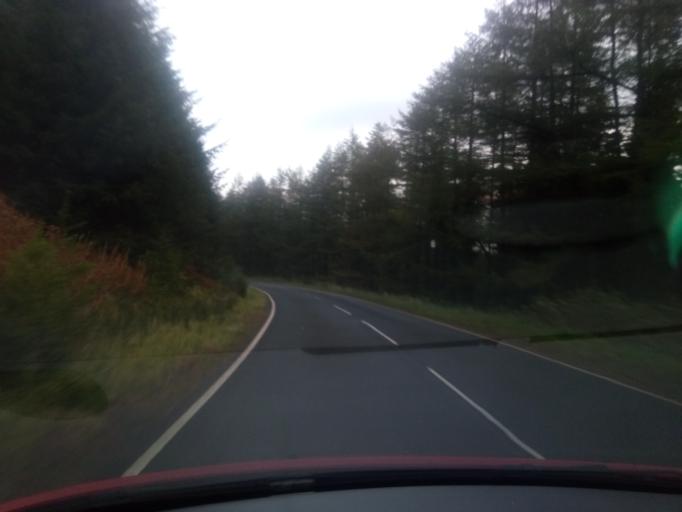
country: GB
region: Scotland
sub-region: The Scottish Borders
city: Hawick
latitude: 55.3326
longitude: -2.6492
